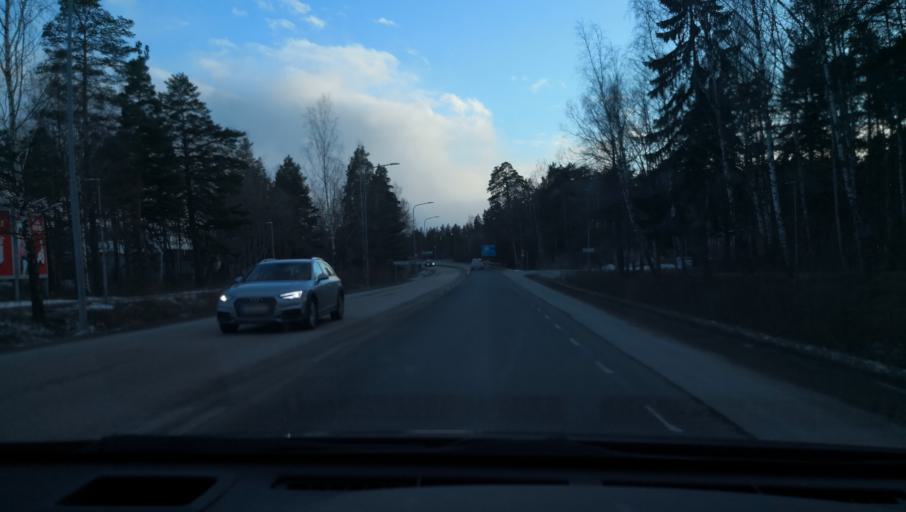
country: SE
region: Vaestmanland
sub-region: Vasteras
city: Vasteras
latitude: 59.6116
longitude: 16.6014
